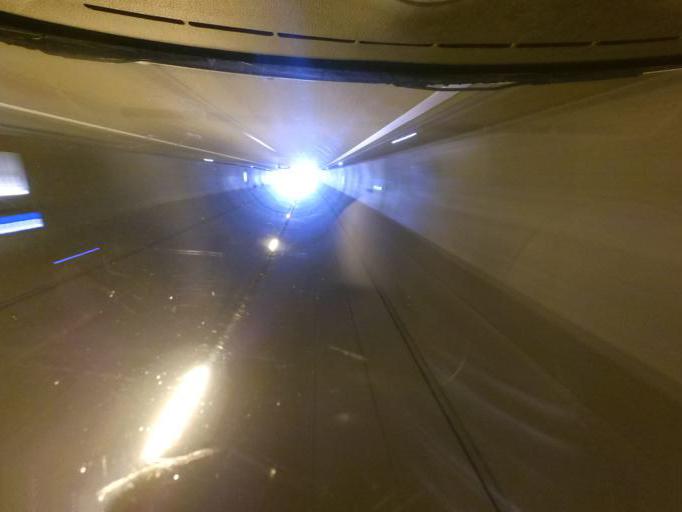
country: DE
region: Saxony
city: Bannewitz
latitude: 51.0212
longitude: 13.6919
